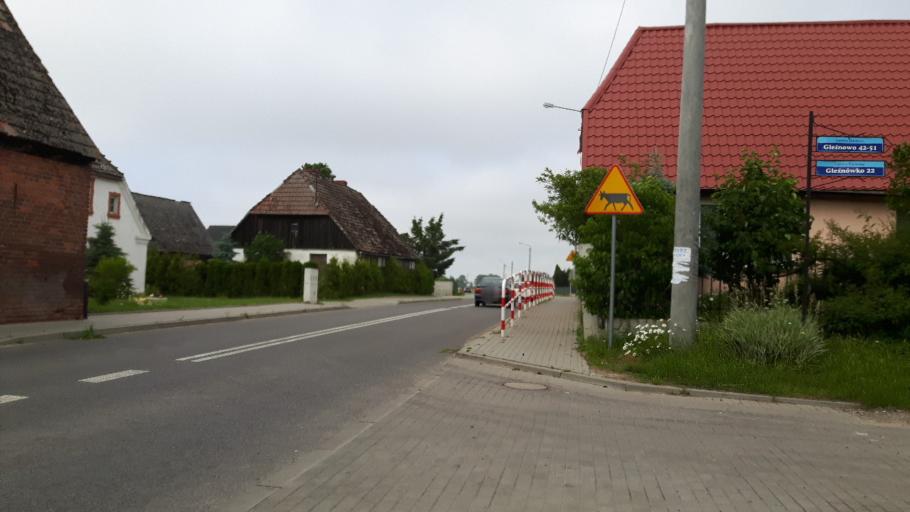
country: PL
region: West Pomeranian Voivodeship
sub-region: Powiat koszalinski
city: Sianow
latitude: 54.3333
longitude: 16.3141
